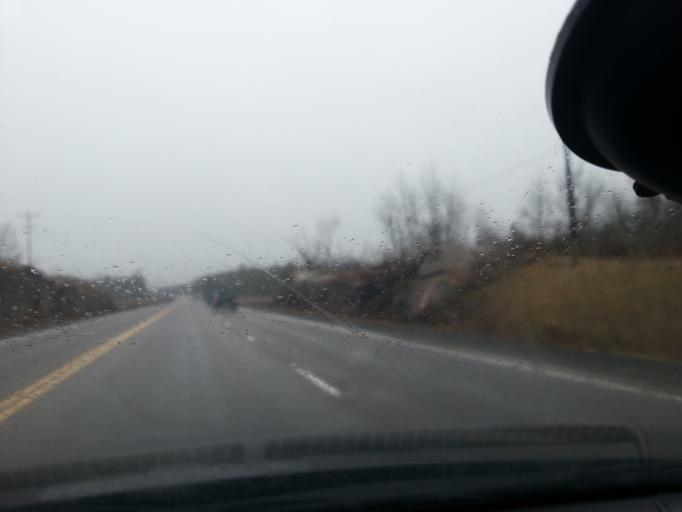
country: CA
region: Ontario
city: Quinte West
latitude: 44.4948
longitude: -77.5655
